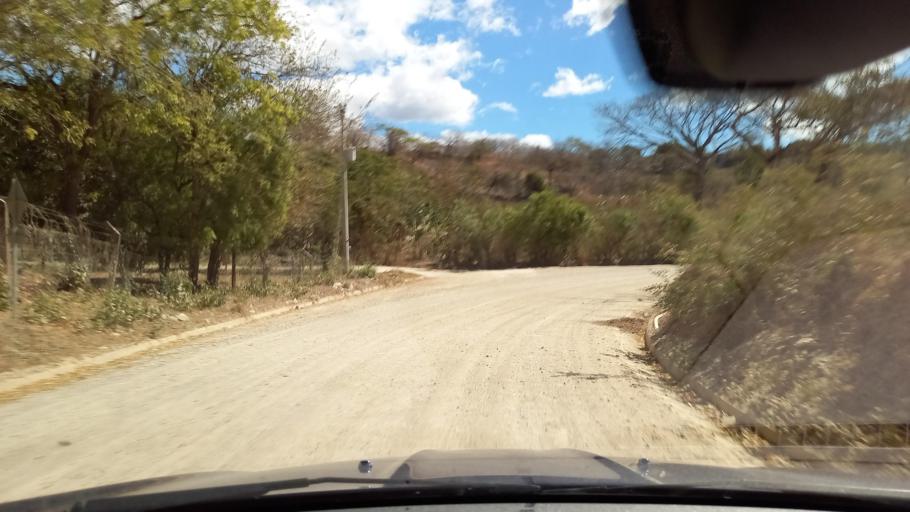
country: SV
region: Santa Ana
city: Metapan
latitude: 14.3621
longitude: -89.4556
